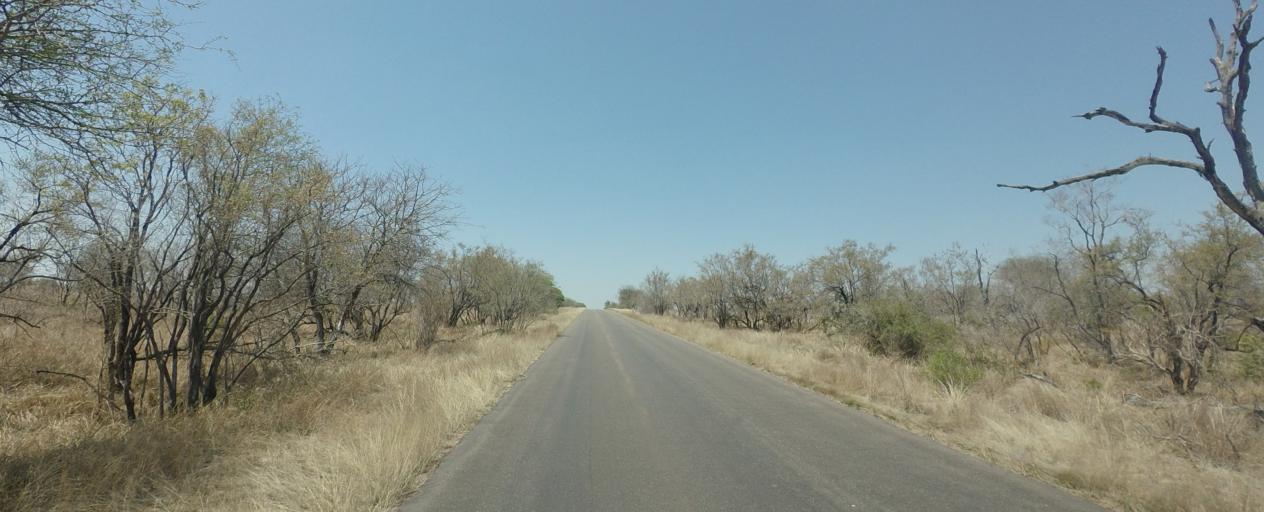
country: ZA
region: Limpopo
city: Thulamahashi
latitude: -24.4729
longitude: 31.4179
